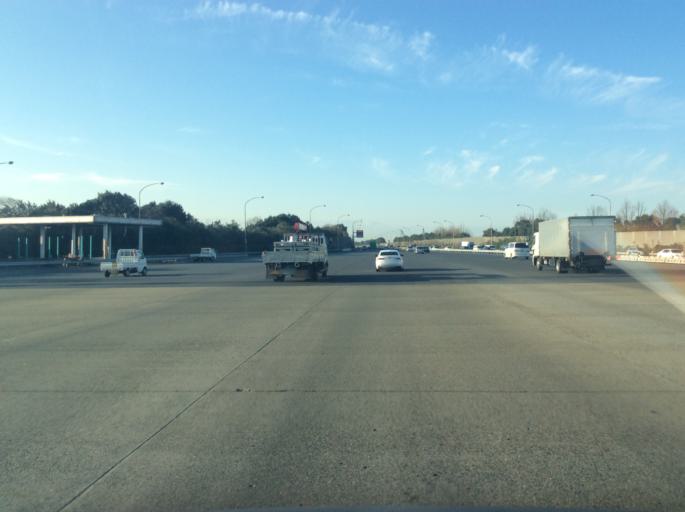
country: JP
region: Chiba
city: Nagareyama
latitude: 35.8652
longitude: 139.8831
